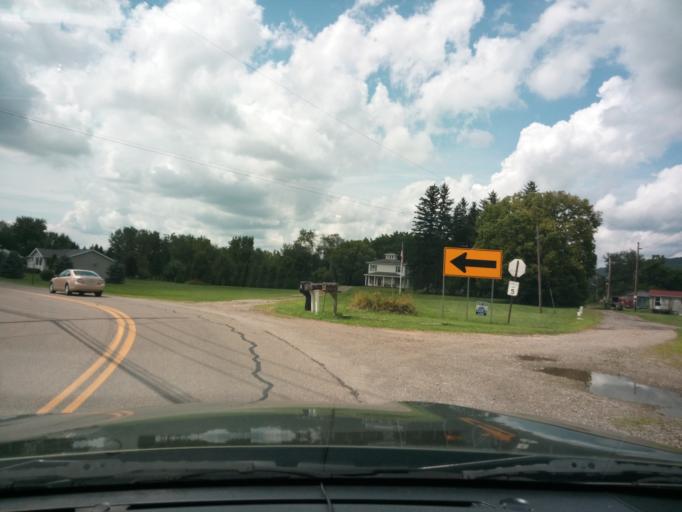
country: US
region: Pennsylvania
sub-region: Bradford County
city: South Waverly
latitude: 41.9958
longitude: -76.5658
